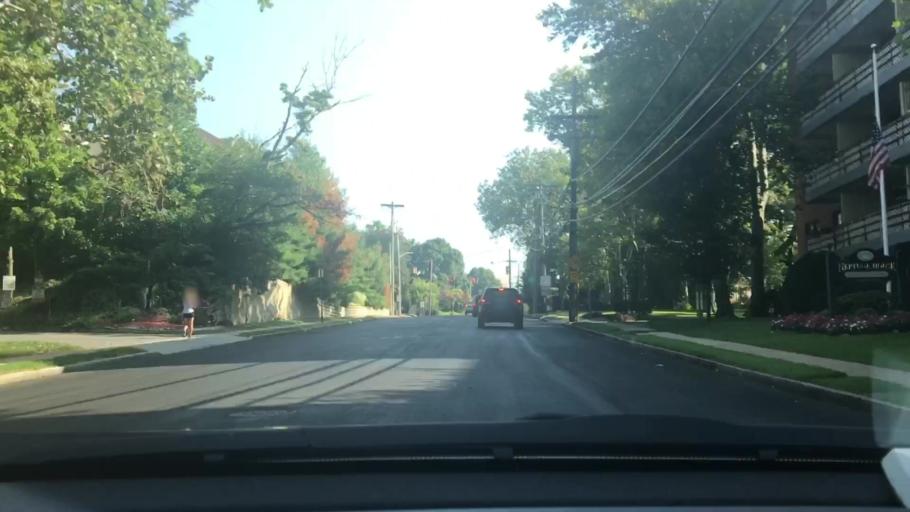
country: US
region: New York
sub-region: Westchester County
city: Pelham Manor
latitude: 40.8907
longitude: -73.7871
